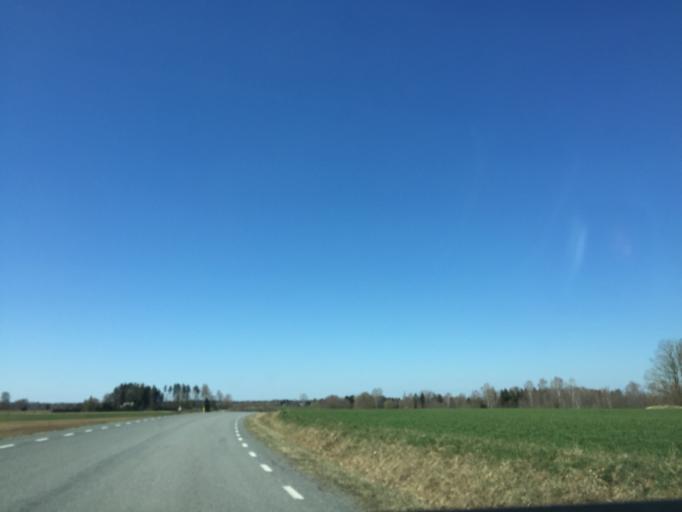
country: EE
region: Viljandimaa
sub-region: Viiratsi vald
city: Viiratsi
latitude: 58.3566
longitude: 25.7332
